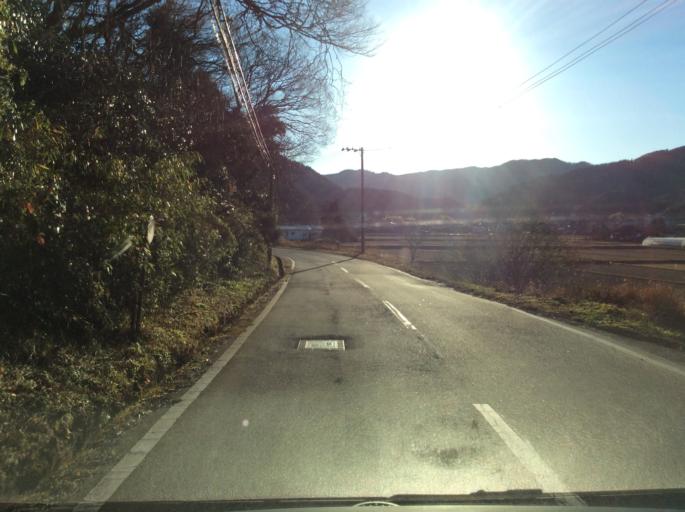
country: JP
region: Ibaraki
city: Kitaibaraki
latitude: 36.9091
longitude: 140.7389
